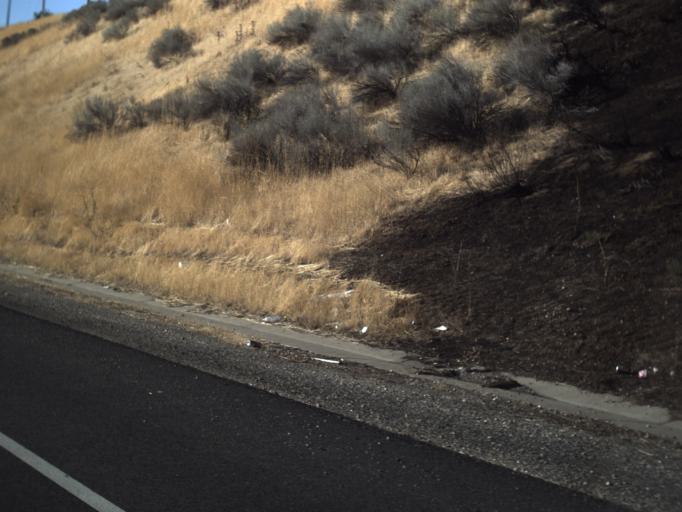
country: US
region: Utah
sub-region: Weber County
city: South Ogden
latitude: 41.2039
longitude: -111.9964
